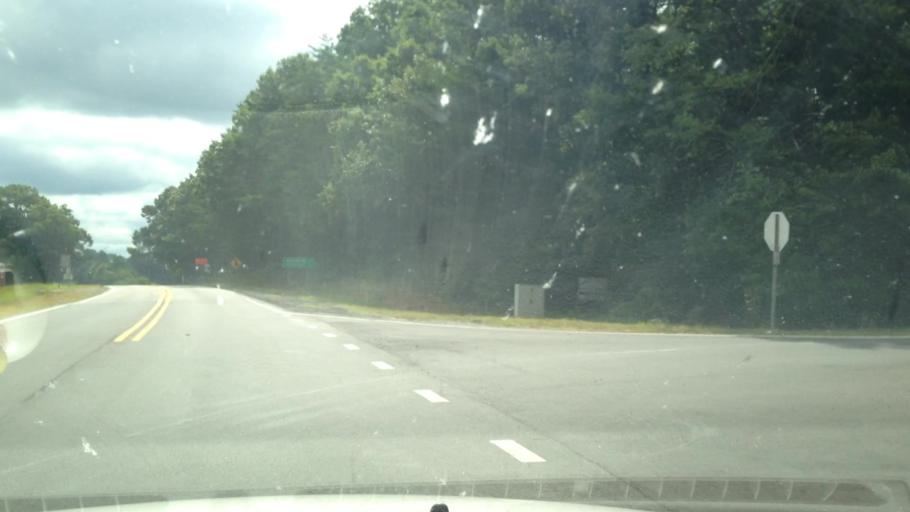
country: US
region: North Carolina
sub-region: Rockingham County
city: Madison
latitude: 36.3747
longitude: -79.9397
